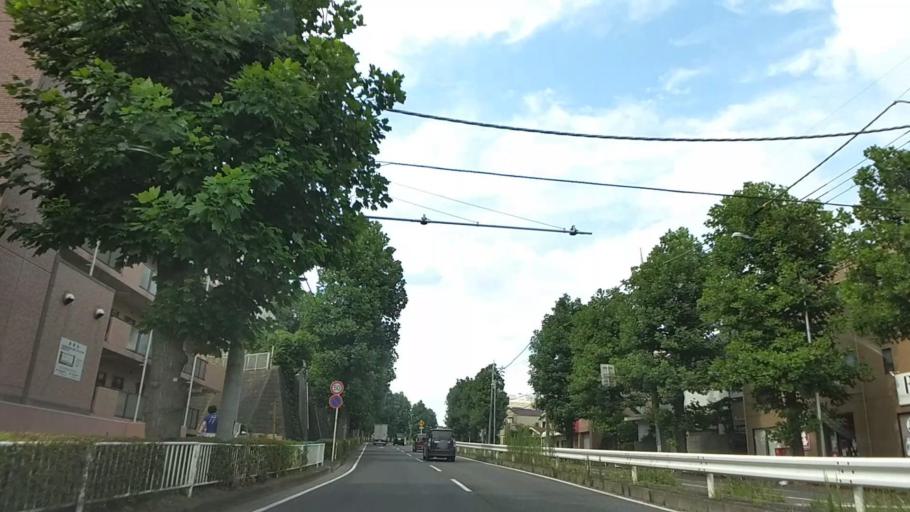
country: JP
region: Kanagawa
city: Yokohama
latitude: 35.5198
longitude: 139.6359
